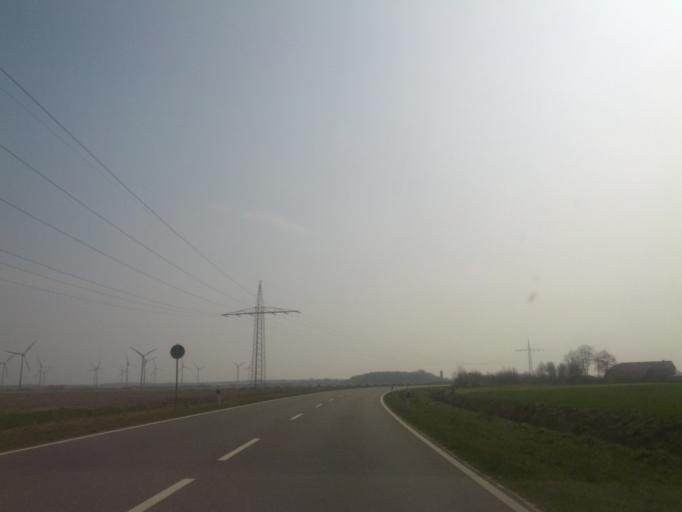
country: DE
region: Lower Saxony
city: Norden
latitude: 53.6137
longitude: 7.2079
